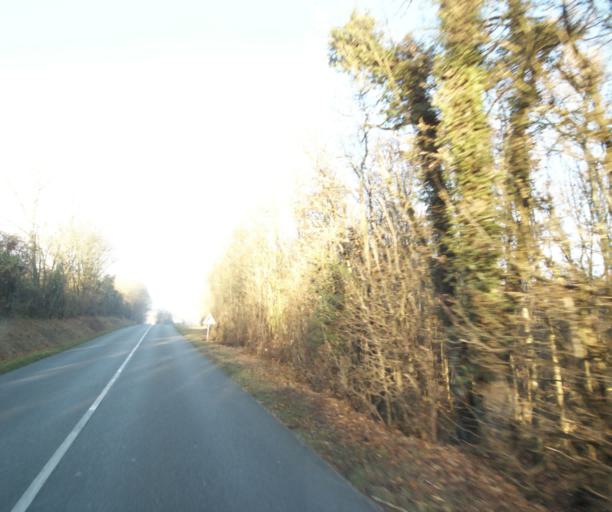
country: FR
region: Poitou-Charentes
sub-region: Departement de la Charente-Maritime
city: Bussac-sur-Charente
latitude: 45.7749
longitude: -0.6221
